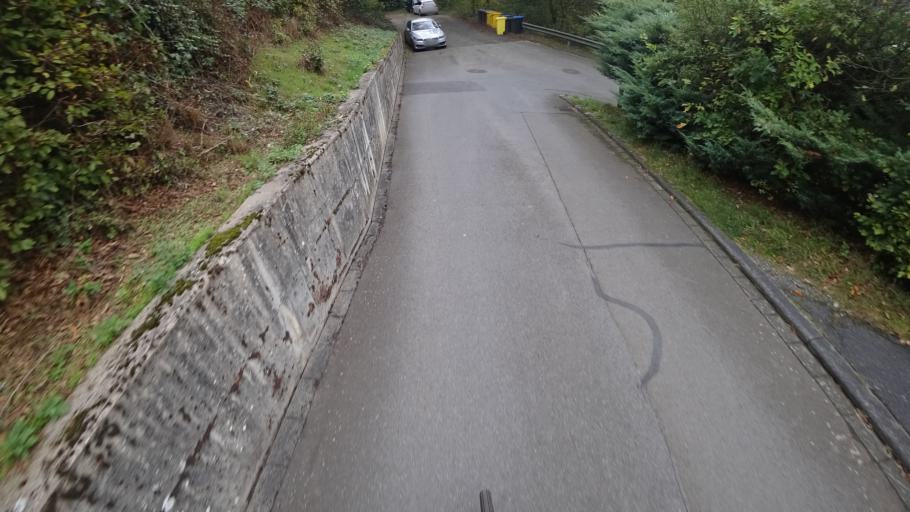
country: DE
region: Rheinland-Pfalz
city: Isselbach
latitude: 50.3902
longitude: 7.8924
